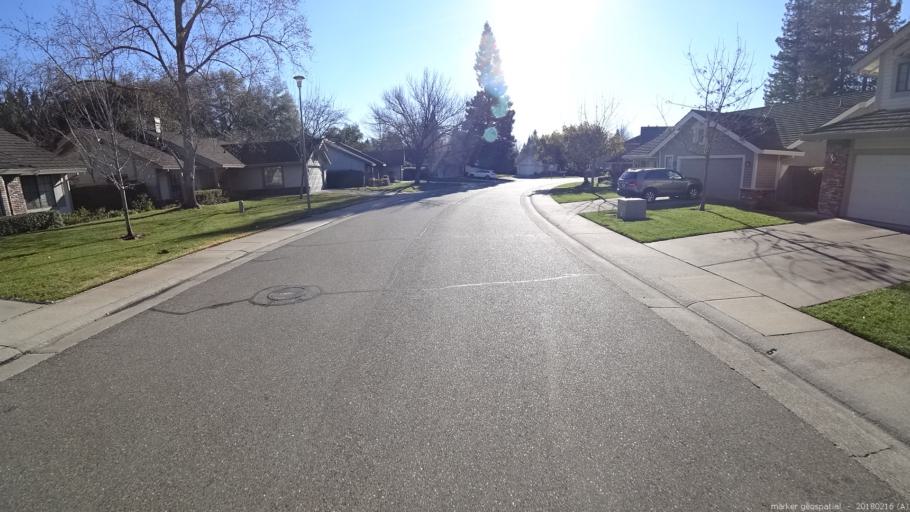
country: US
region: California
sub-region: Sacramento County
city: Gold River
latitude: 38.6278
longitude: -121.2449
